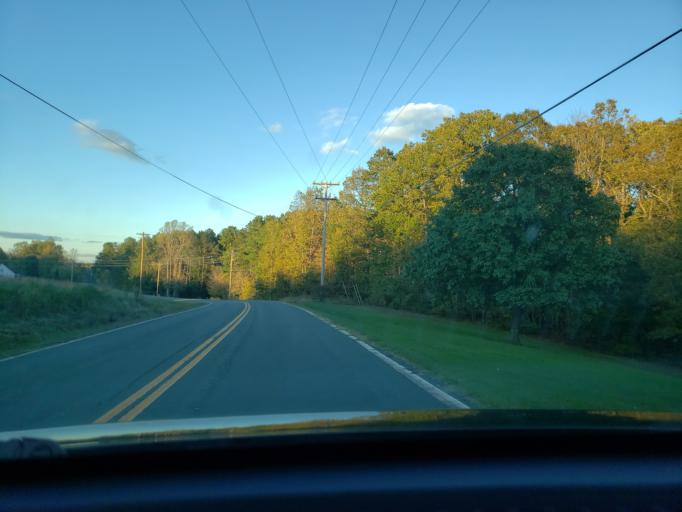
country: US
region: North Carolina
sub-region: Stokes County
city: Danbury
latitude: 36.3691
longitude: -80.1903
